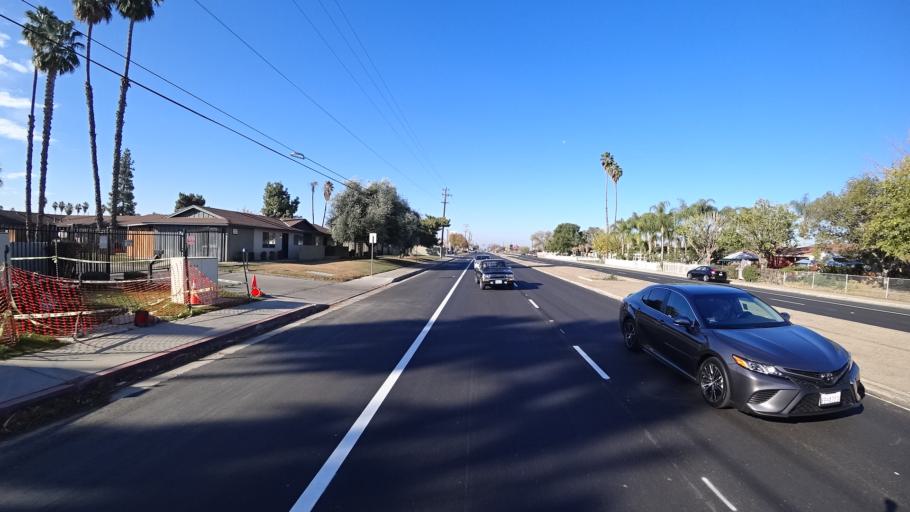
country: US
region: California
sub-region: Kern County
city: Greenfield
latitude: 35.3176
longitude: -119.0179
